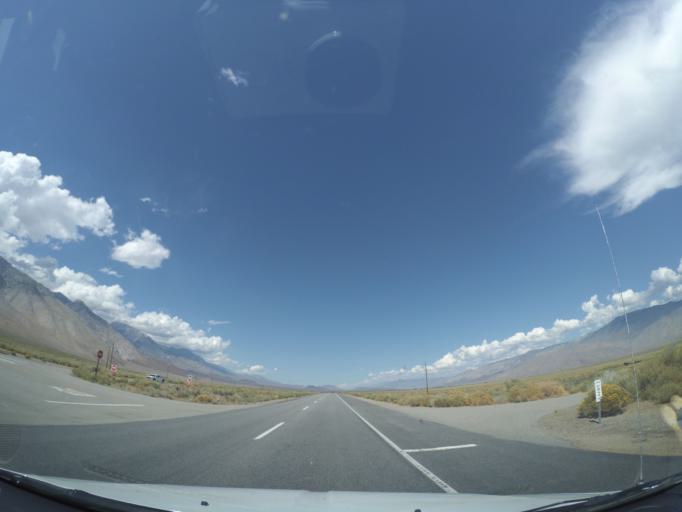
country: US
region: California
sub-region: Inyo County
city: Big Pine
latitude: 36.8758
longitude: -118.2382
